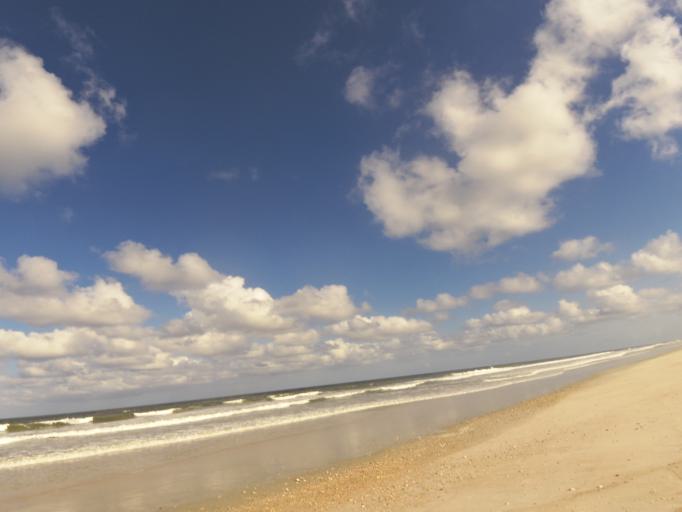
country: US
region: Florida
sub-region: Saint Johns County
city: Palm Valley
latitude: 30.0702
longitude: -81.3653
